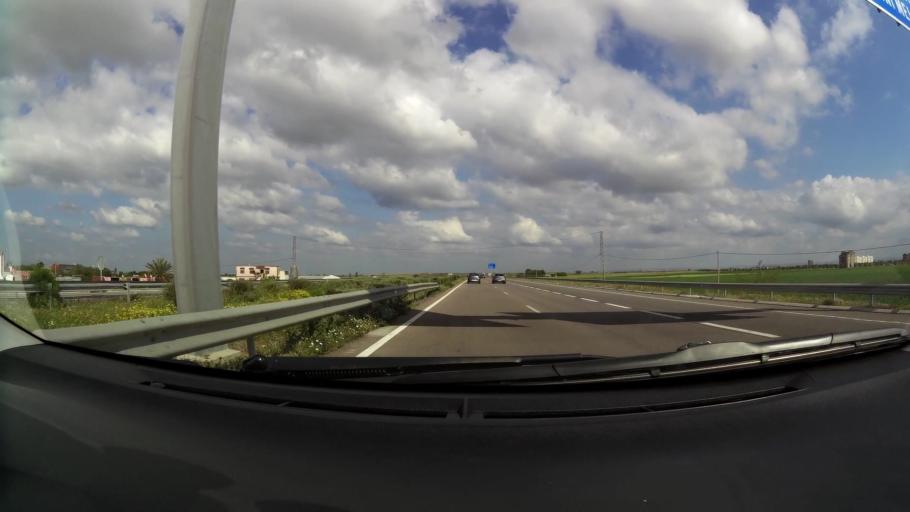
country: MA
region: Chaouia-Ouardigha
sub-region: Settat Province
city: Berrechid
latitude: 33.3009
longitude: -7.5689
